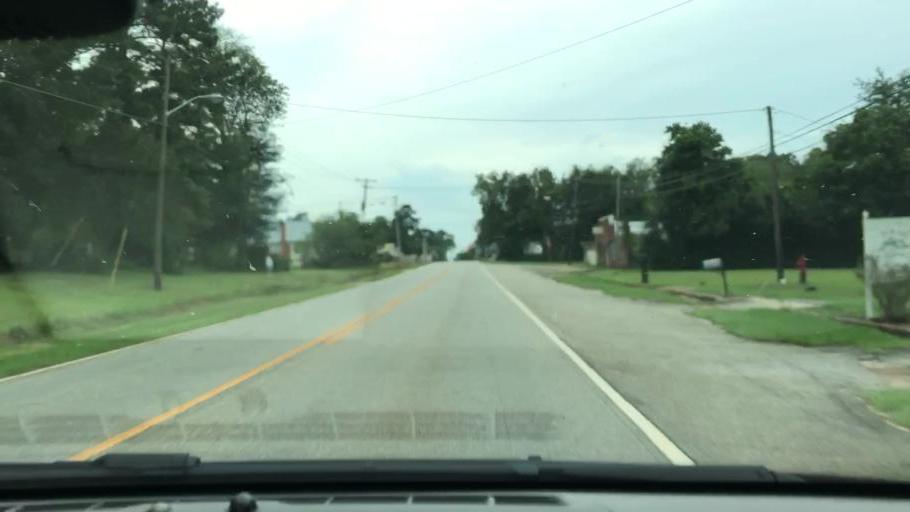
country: US
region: Georgia
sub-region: Early County
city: Blakely
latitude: 31.3944
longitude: -84.9330
